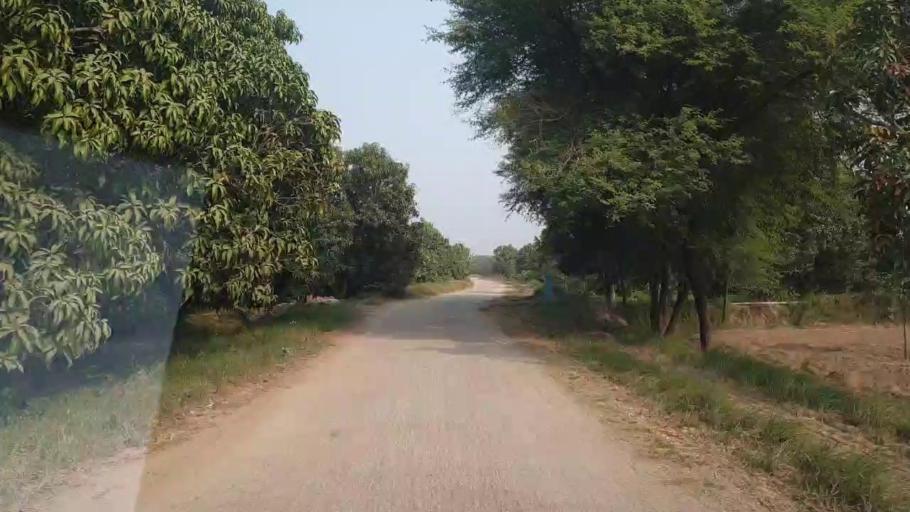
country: PK
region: Sindh
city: Tando Jam
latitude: 25.3319
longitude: 68.5180
